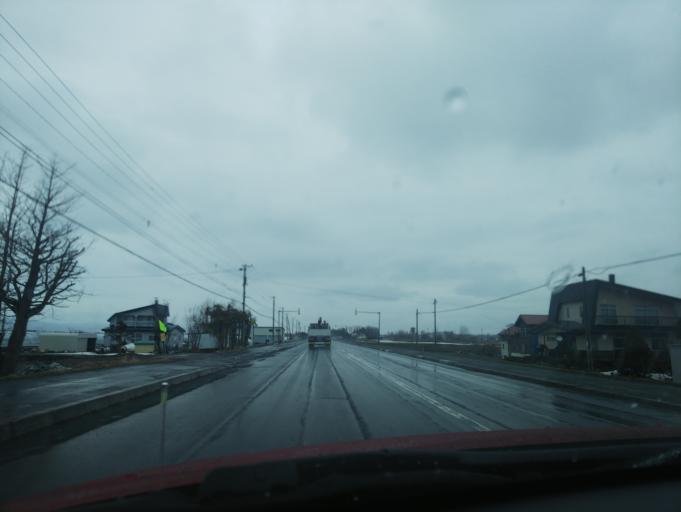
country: JP
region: Hokkaido
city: Nayoro
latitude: 44.2123
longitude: 142.3949
